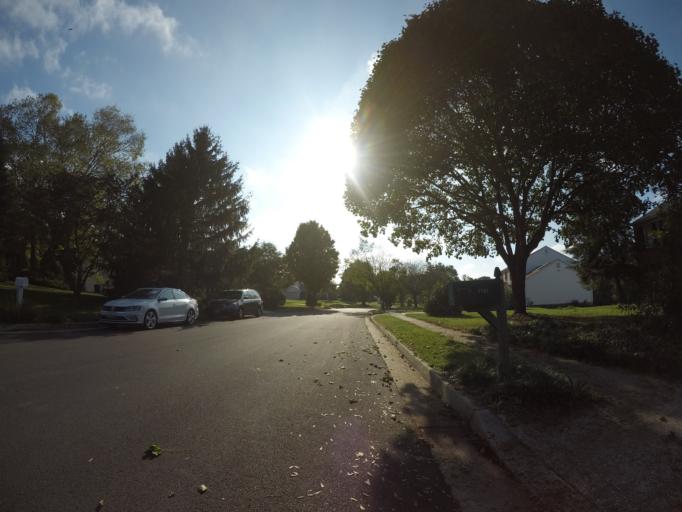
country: US
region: Maryland
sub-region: Howard County
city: Columbia
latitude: 39.2688
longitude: -76.8451
